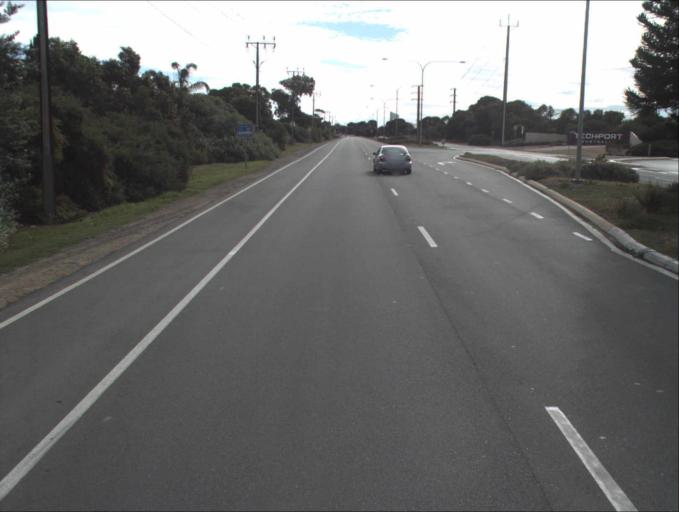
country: AU
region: South Australia
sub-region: Port Adelaide Enfield
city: Birkenhead
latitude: -34.7905
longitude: 138.5014
